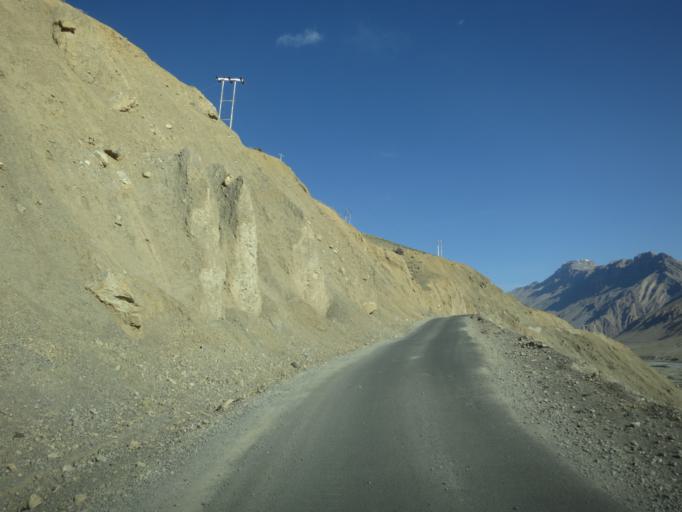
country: IN
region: Himachal Pradesh
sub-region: Shimla
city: Sarahan
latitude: 32.2401
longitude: 78.0596
